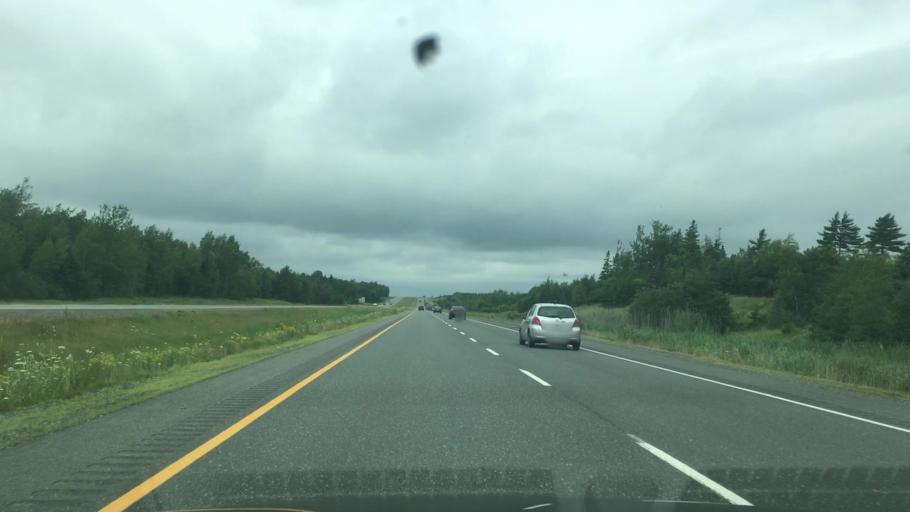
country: CA
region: Nova Scotia
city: Truro
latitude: 45.3861
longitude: -63.3781
